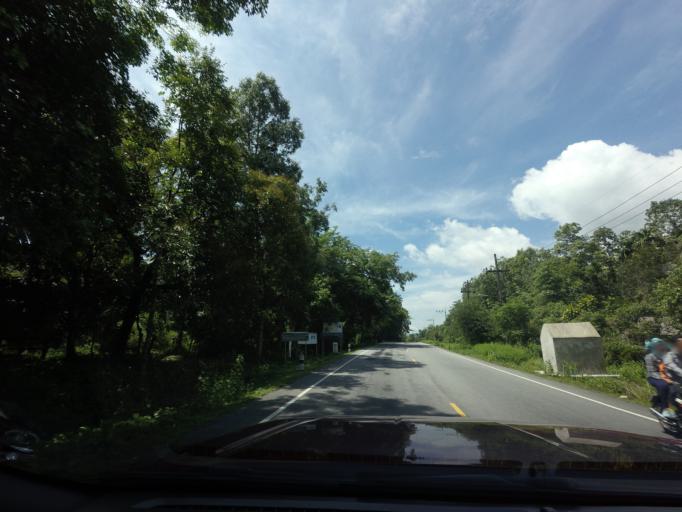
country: TH
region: Narathiwat
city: Rueso
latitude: 6.3622
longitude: 101.6093
